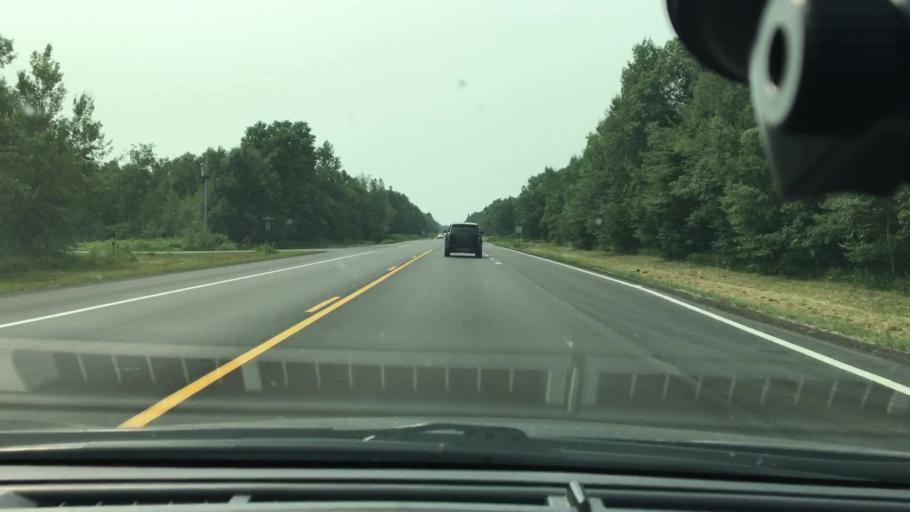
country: US
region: Minnesota
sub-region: Crow Wing County
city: Brainerd
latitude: 46.4571
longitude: -94.1723
